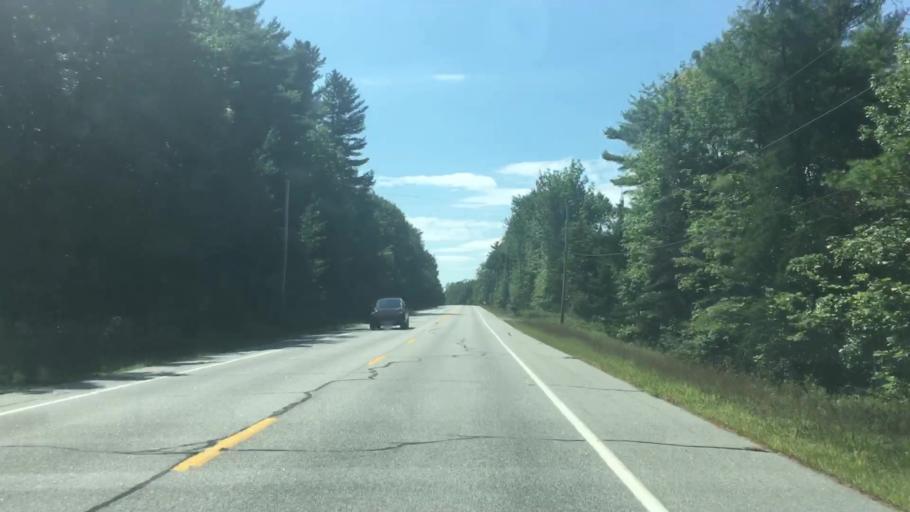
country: US
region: Maine
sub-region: Androscoggin County
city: Sabattus
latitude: 44.1379
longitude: -70.0561
